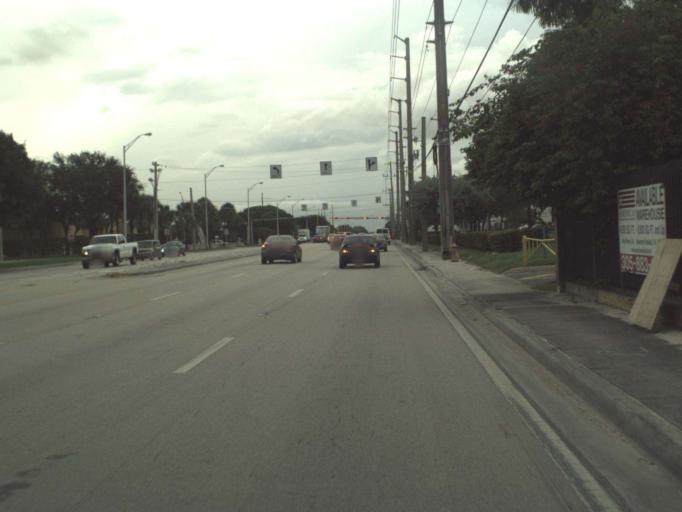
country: US
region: Florida
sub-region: Miami-Dade County
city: Virginia Gardens
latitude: 25.8242
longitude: -80.3136
